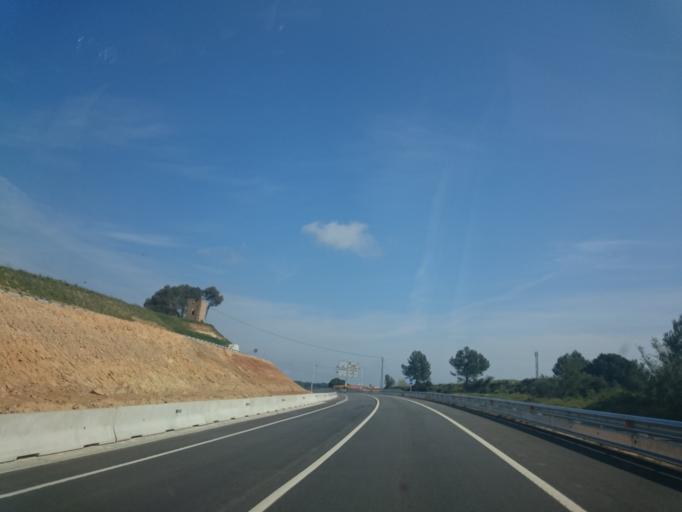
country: ES
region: Catalonia
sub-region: Provincia de Girona
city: Cervia de Ter
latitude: 42.0922
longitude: 2.8924
